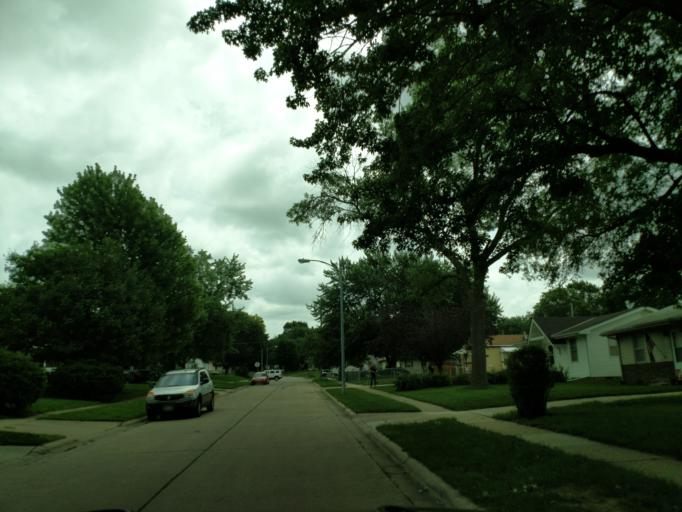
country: US
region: Nebraska
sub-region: Sarpy County
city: La Vista
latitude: 41.2093
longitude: -95.9991
